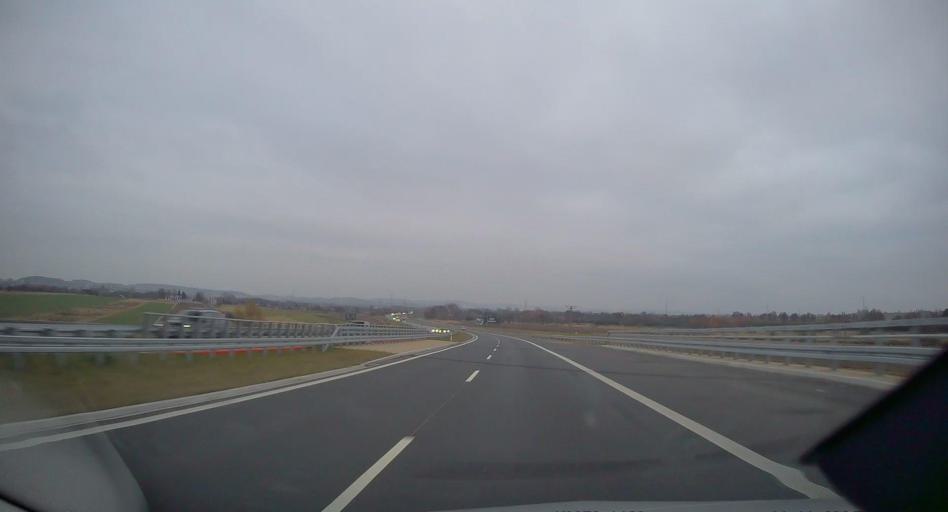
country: PL
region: Silesian Voivodeship
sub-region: Powiat bedzinski
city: Mierzecice
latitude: 50.4258
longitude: 19.1625
